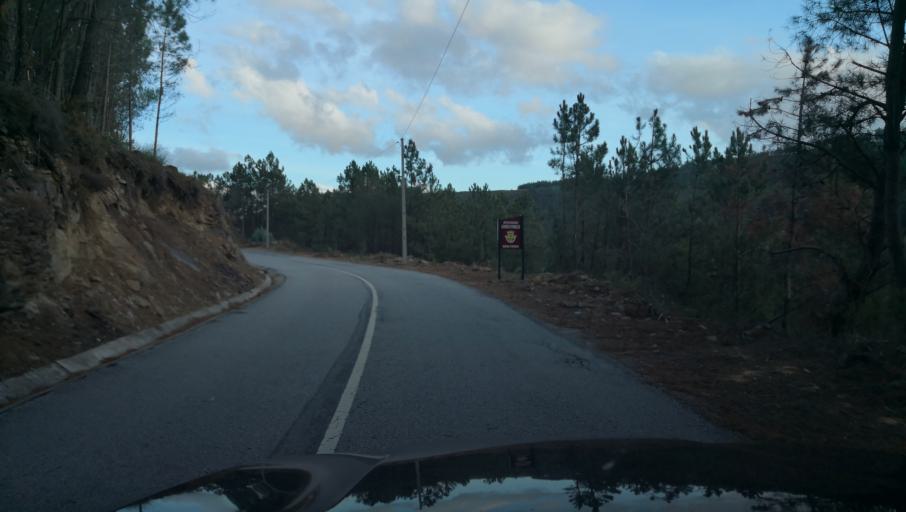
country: PT
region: Vila Real
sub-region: Santa Marta de Penaguiao
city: Santa Marta de Penaguiao
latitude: 41.2438
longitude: -7.8474
